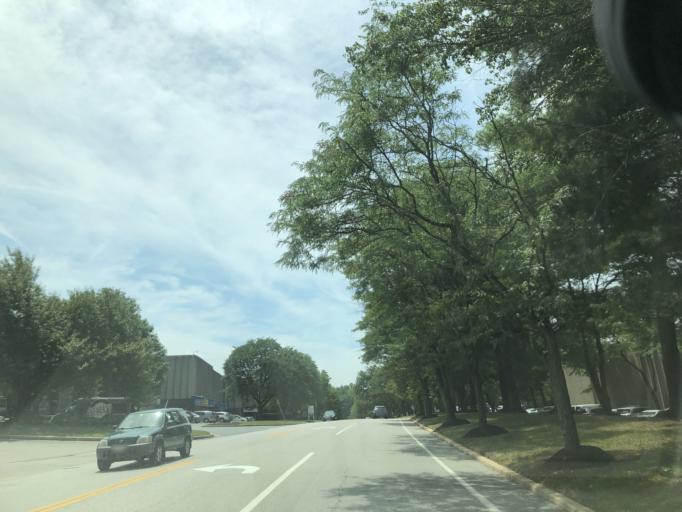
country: US
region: Maryland
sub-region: Howard County
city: Savage
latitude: 39.1880
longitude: -76.8234
